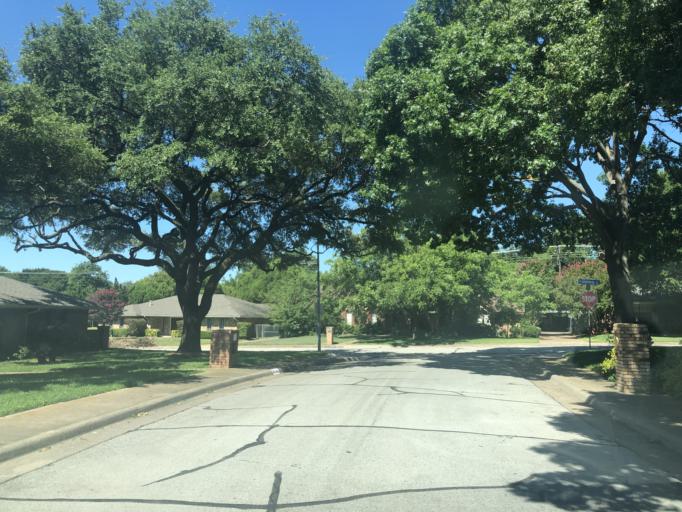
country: US
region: Texas
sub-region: Dallas County
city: Duncanville
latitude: 32.6385
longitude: -96.9296
